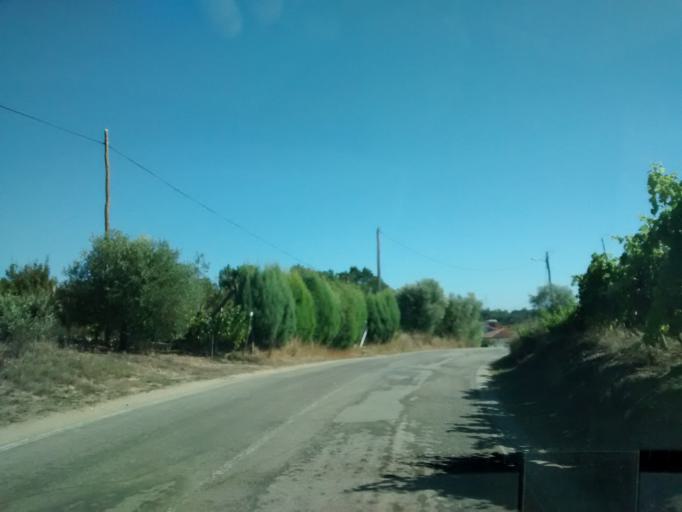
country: PT
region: Aveiro
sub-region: Anadia
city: Sangalhos
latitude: 40.4421
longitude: -8.5013
